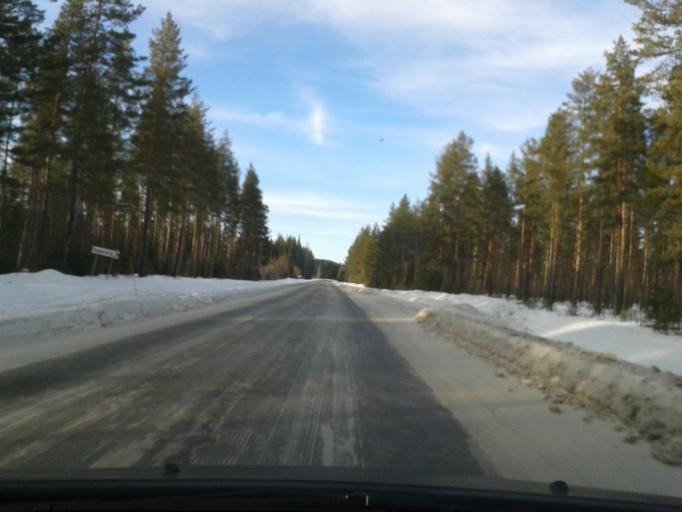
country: SE
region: Vaesternorrland
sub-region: OErnskoeldsviks Kommun
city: Bredbyn
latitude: 63.5385
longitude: 17.9626
